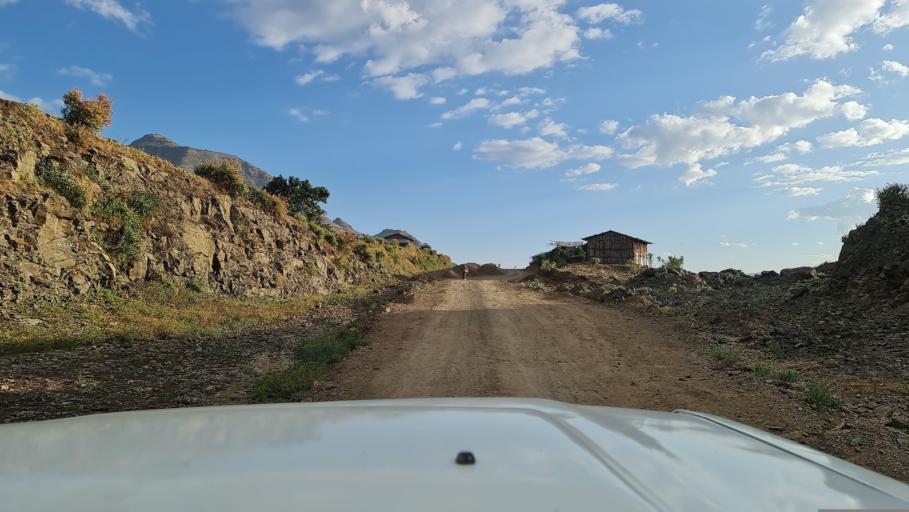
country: ET
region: Amhara
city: Debark'
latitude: 13.0405
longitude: 38.0384
